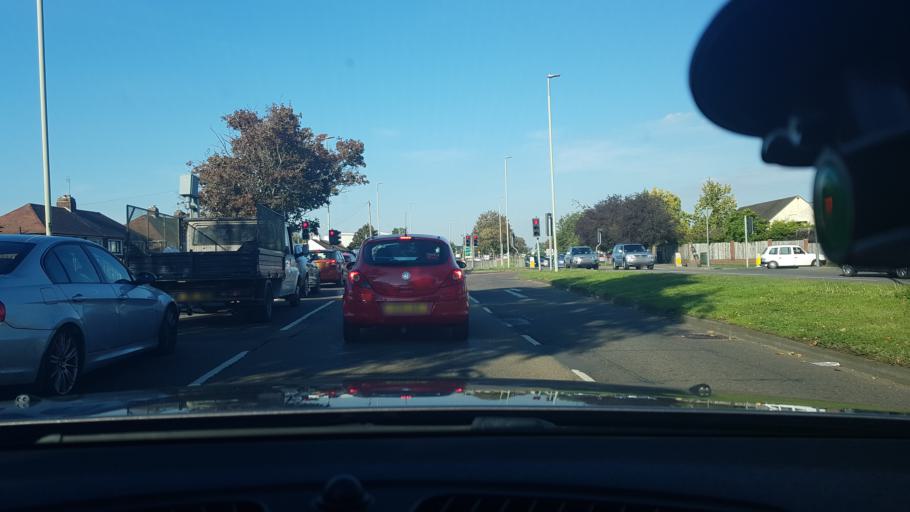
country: GB
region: England
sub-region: Gloucestershire
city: Gloucester
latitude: 51.8538
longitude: -2.2245
